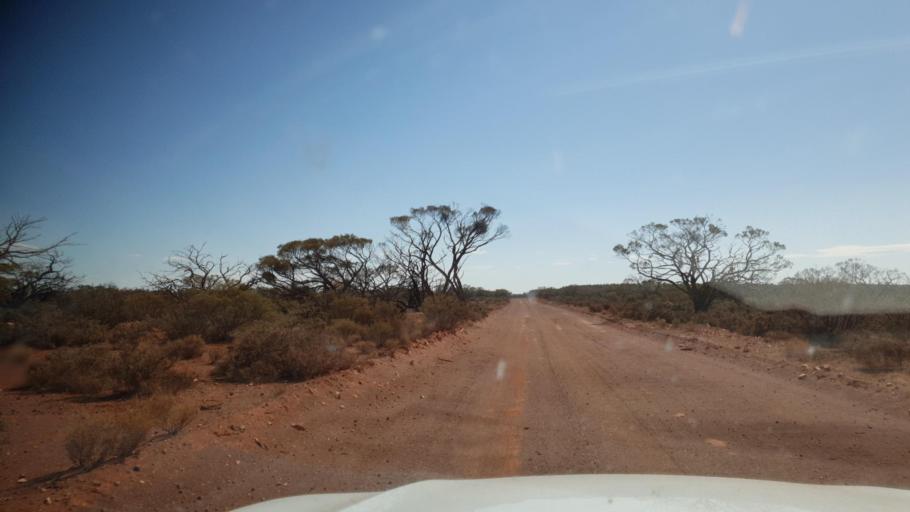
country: AU
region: South Australia
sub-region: Kimba
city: Caralue
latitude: -32.5210
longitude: 136.1354
